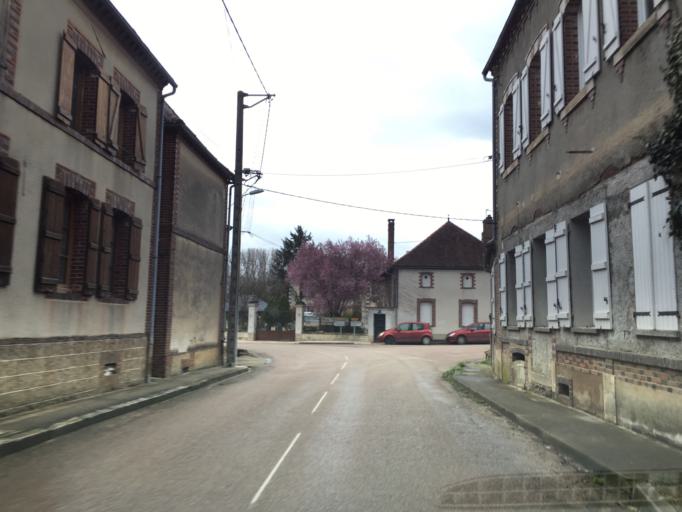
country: FR
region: Bourgogne
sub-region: Departement de l'Yonne
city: Pourrain
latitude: 47.8070
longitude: 3.3660
